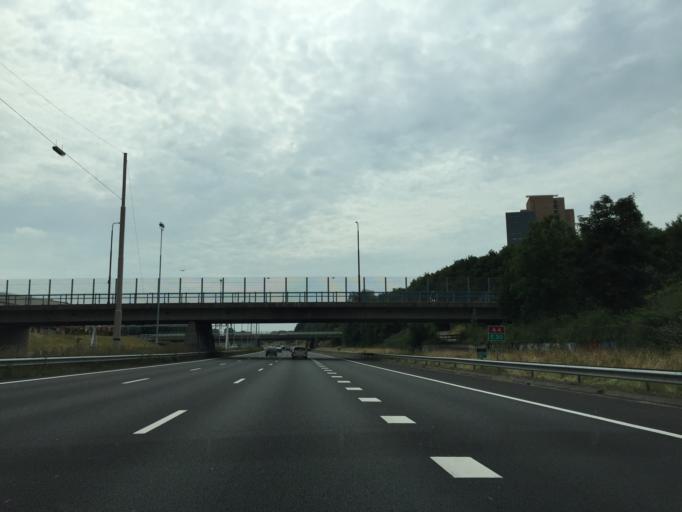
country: NL
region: South Holland
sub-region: Gemeente Rijswijk
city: Rijswijk
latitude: 52.0336
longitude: 4.3319
